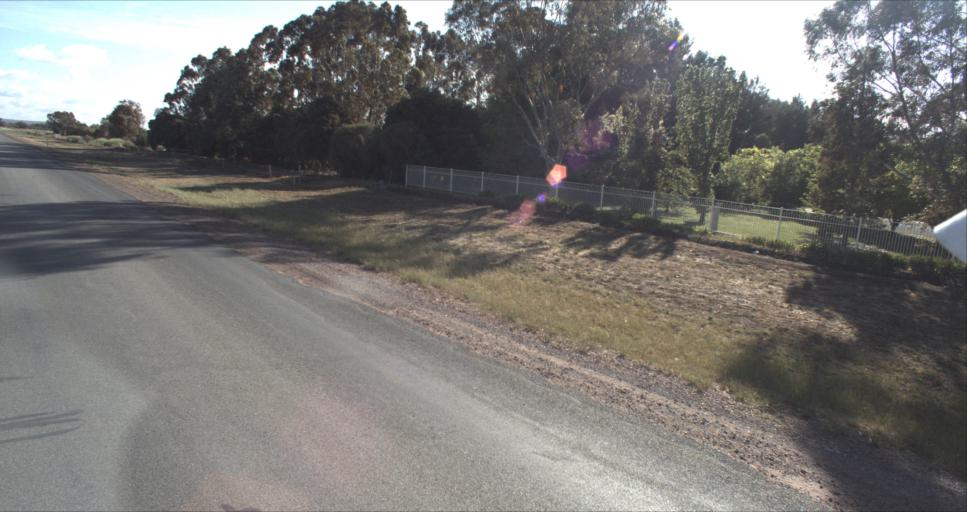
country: AU
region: New South Wales
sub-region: Leeton
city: Leeton
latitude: -34.5296
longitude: 146.3890
